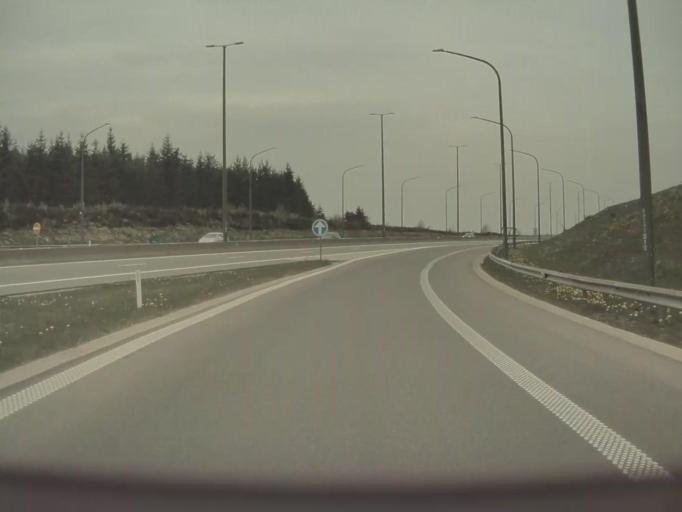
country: BE
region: Wallonia
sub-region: Province du Luxembourg
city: Manhay
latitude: 50.2497
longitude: 5.7305
